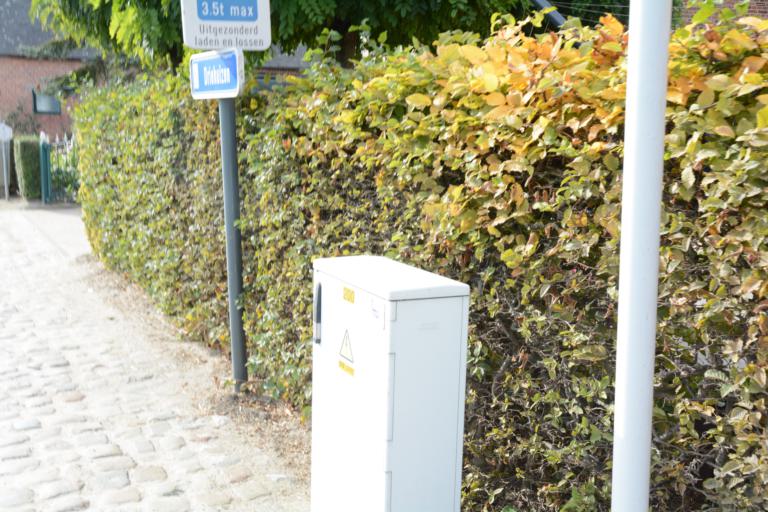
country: BE
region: Flanders
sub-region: Provincie Antwerpen
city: Sint-Amands
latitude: 51.0344
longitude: 4.2344
